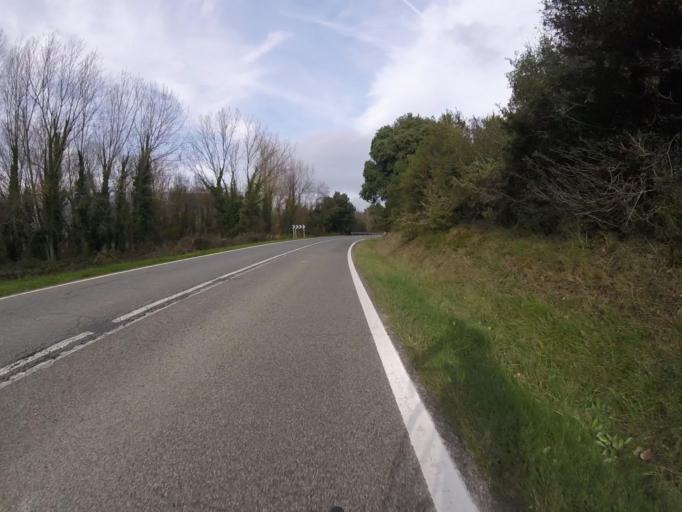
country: ES
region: Navarre
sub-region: Provincia de Navarra
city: Estella
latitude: 42.7059
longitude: -2.0681
